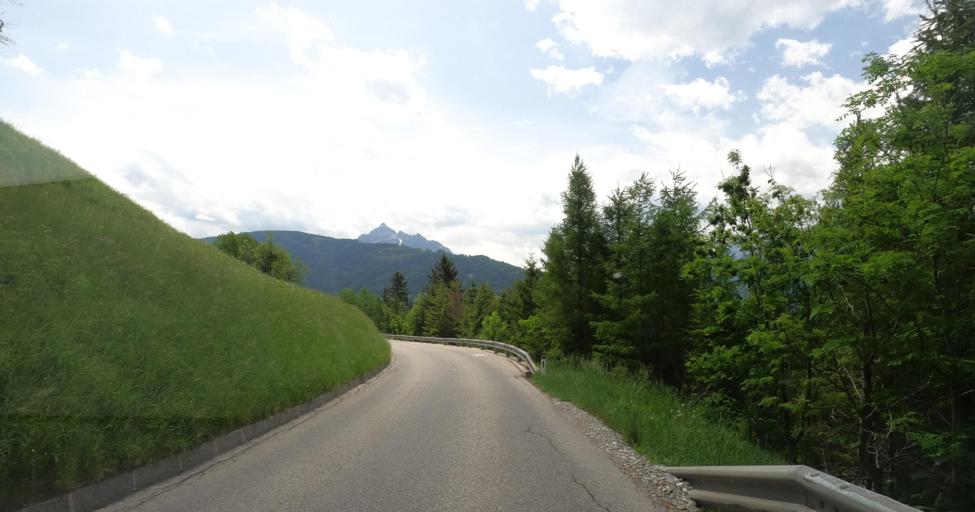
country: AT
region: Tyrol
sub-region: Politischer Bezirk Innsbruck Land
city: Patsch
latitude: 47.1966
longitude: 11.4237
